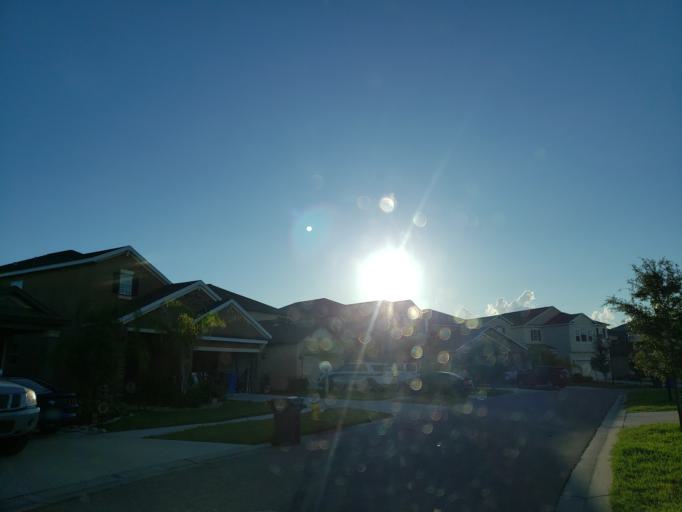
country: US
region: Florida
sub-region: Hillsborough County
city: Ruskin
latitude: 27.7289
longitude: -82.4077
